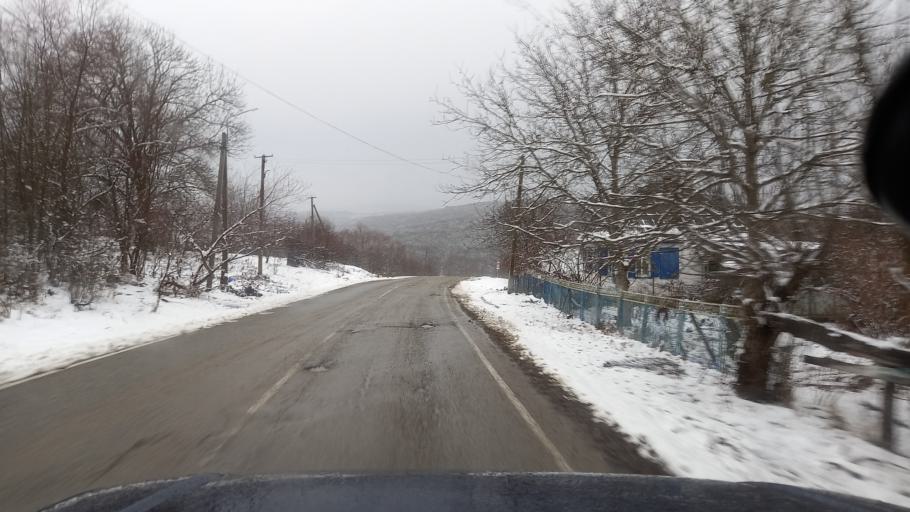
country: RU
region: Adygeya
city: Abadzekhskaya
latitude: 44.3574
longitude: 40.4076
